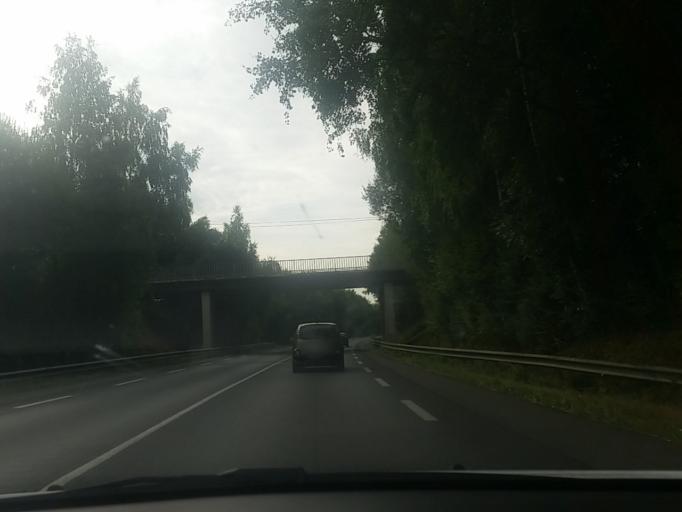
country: FR
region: Pays de la Loire
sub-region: Departement de la Vendee
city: Saint-Fulgent
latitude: 46.8527
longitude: -1.1650
